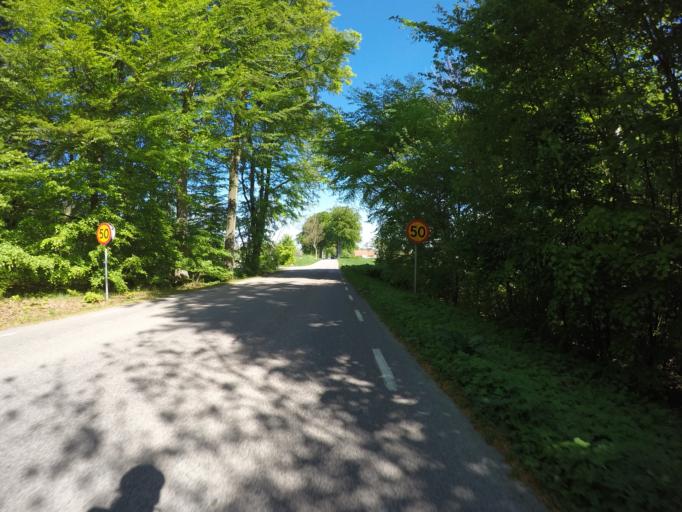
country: SE
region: Skane
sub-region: Svedala Kommun
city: Klagerup
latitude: 55.5605
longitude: 13.2139
